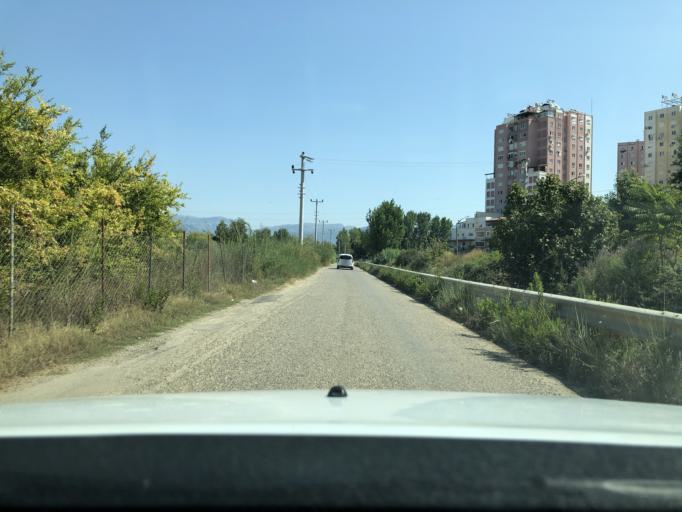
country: TR
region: Antalya
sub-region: Manavgat
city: Manavgat
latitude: 36.7963
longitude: 31.4641
